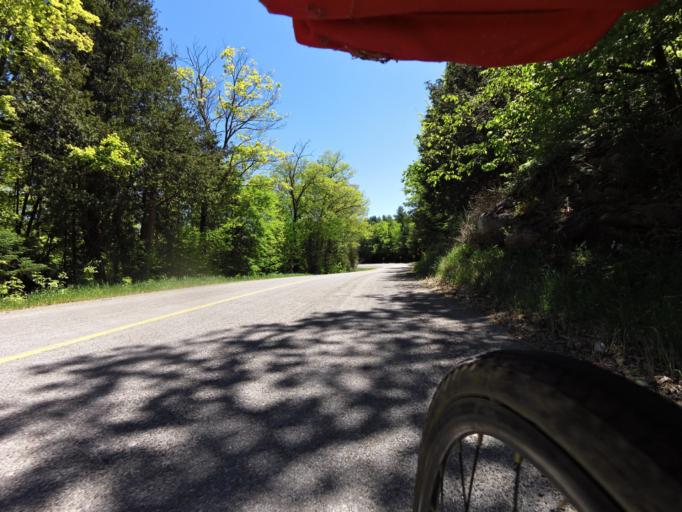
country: CA
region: Ontario
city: Arnprior
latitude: 45.1612
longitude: -76.4399
